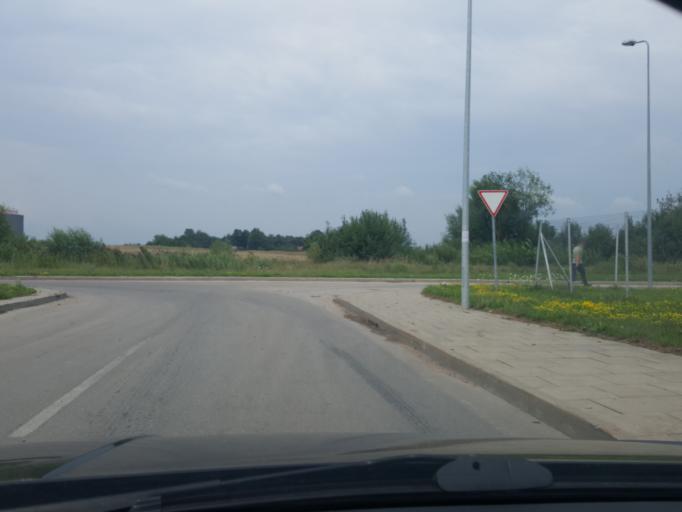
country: LT
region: Alytaus apskritis
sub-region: Alytus
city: Alytus
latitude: 54.4376
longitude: 24.0262
